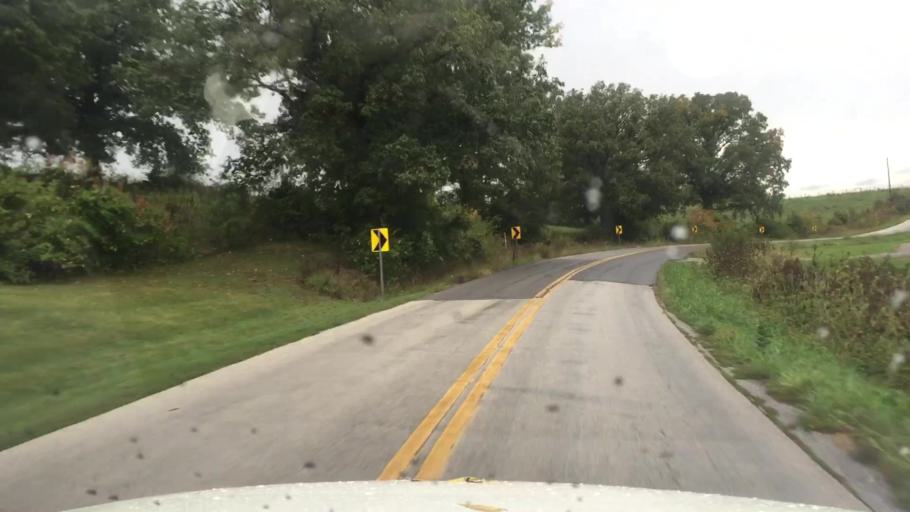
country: US
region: Missouri
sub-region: Boone County
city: Columbia
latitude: 38.9243
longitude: -92.4685
